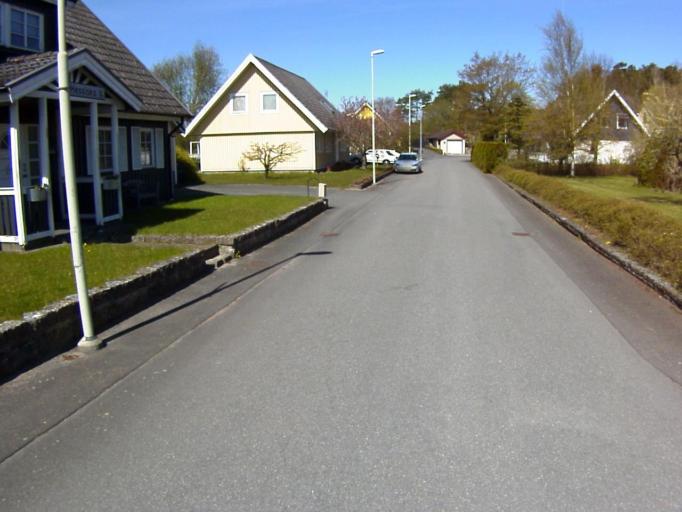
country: SE
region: Skane
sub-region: Kristianstads Kommun
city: Norra Asum
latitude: 55.9959
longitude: 14.0788
